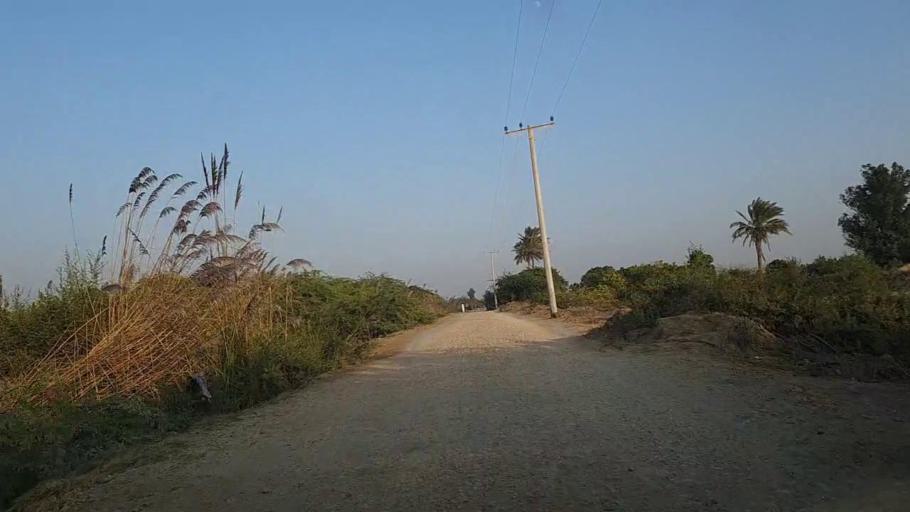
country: PK
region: Sindh
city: Keti Bandar
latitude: 24.2769
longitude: 67.6541
